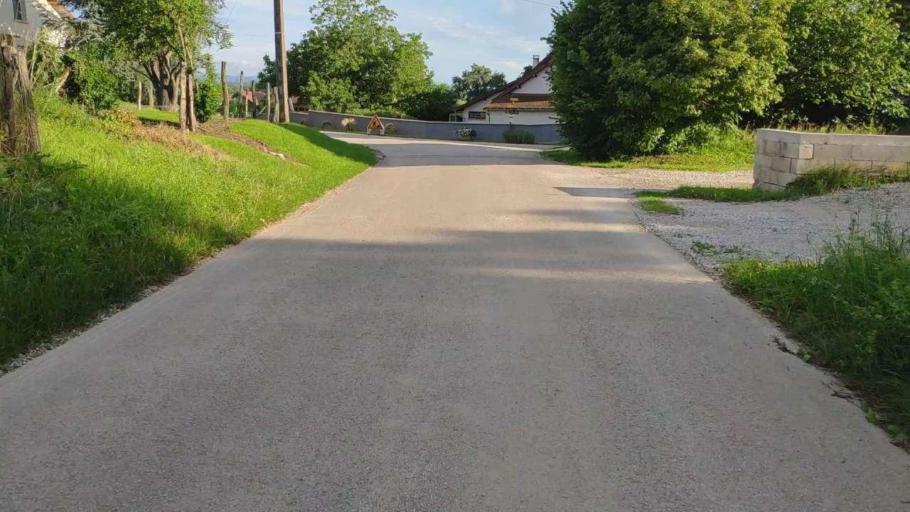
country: FR
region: Franche-Comte
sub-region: Departement du Jura
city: Bletterans
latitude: 46.7809
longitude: 5.4930
